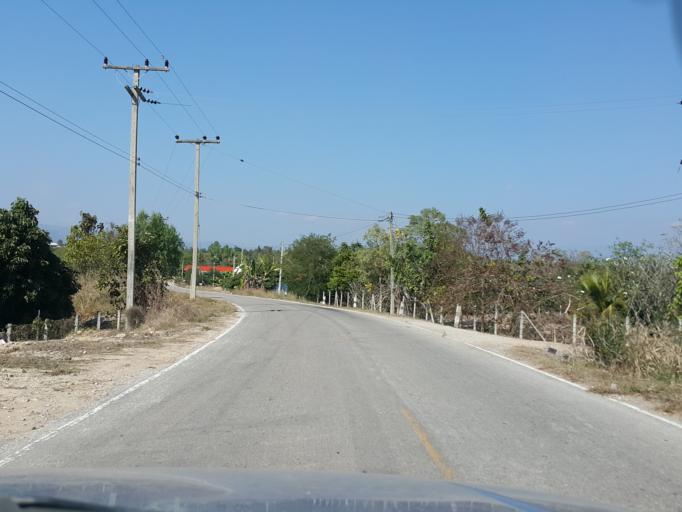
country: TH
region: Chiang Mai
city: Mae Wang
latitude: 18.5519
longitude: 98.7963
